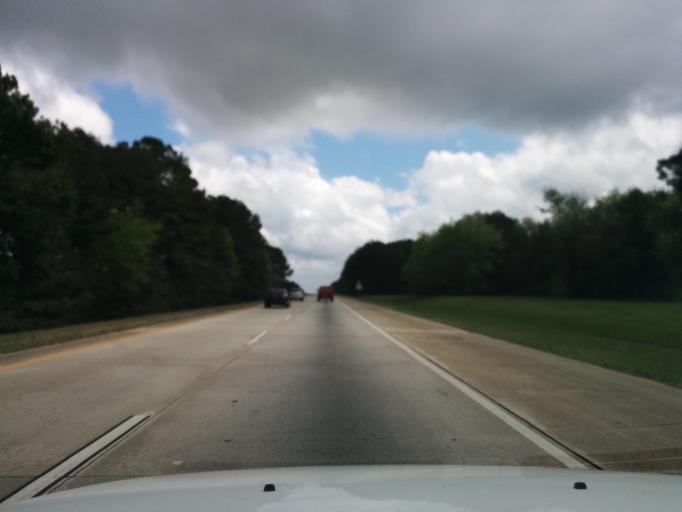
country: US
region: Georgia
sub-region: Bulloch County
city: Statesboro
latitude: 32.2893
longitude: -81.8023
